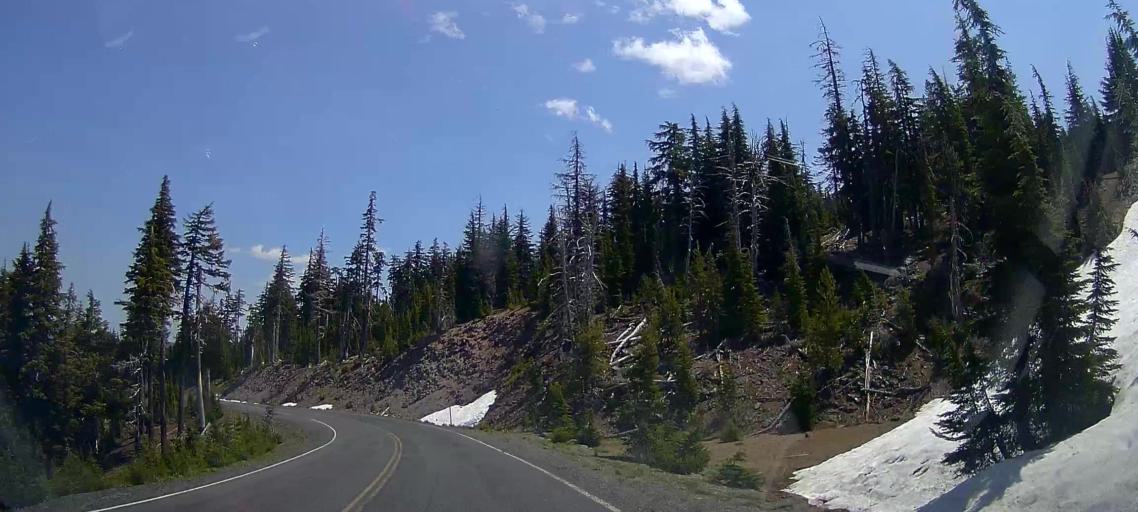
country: US
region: Oregon
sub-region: Jackson County
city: Shady Cove
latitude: 42.9857
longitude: -122.1468
